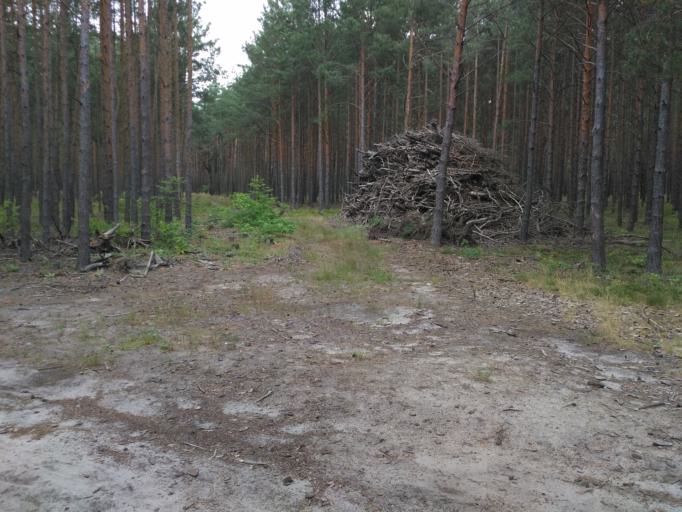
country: DE
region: Saxony
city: Hoyerswerda
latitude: 51.4546
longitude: 14.2814
